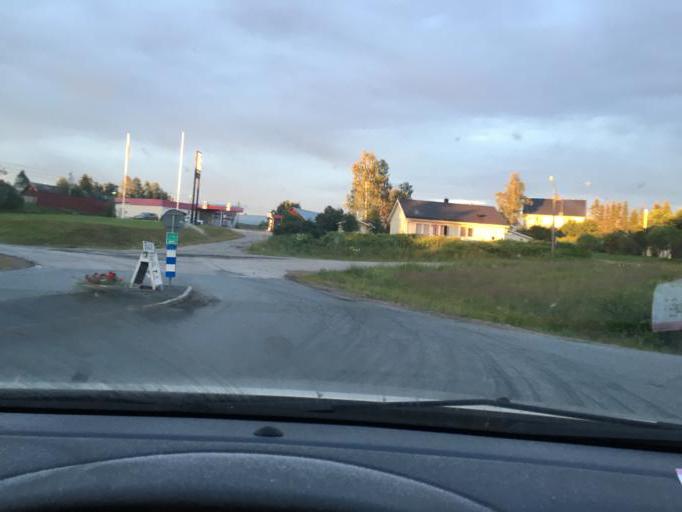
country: SE
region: Norrbotten
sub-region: Kalix Kommun
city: Toere
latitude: 66.0695
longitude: 22.7069
